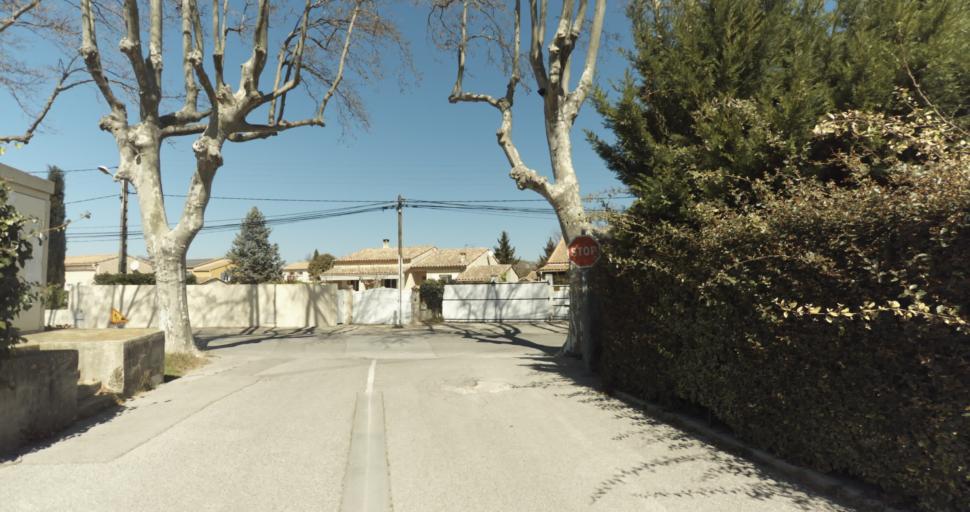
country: FR
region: Provence-Alpes-Cote d'Azur
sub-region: Departement des Bouches-du-Rhone
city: Pelissanne
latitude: 43.6281
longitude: 5.1614
